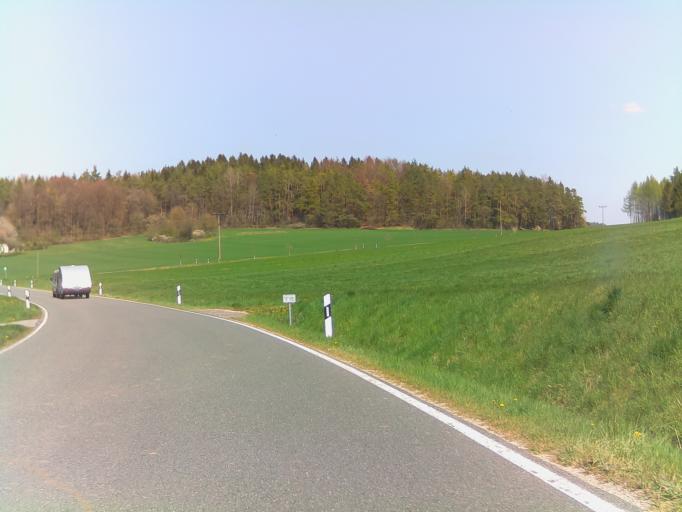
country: DE
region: Bavaria
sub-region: Upper Palatinate
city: Weigendorf
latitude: 49.4803
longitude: 11.5554
